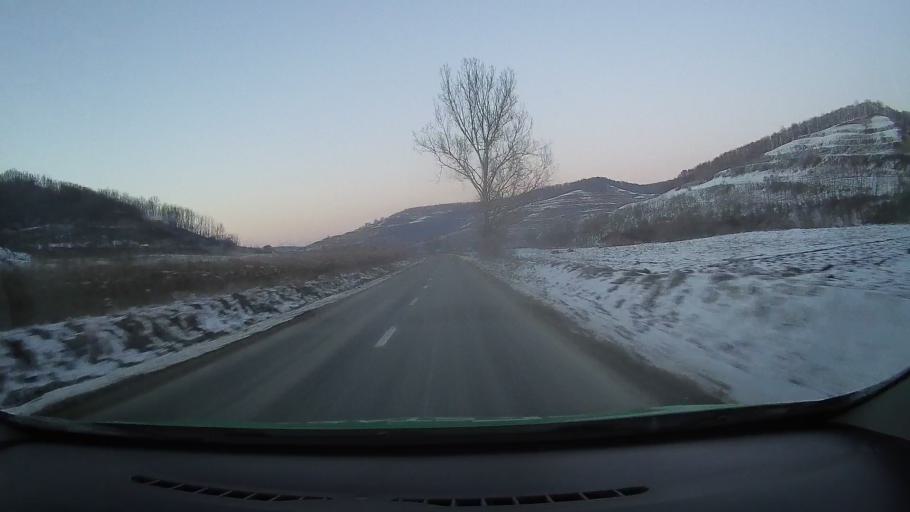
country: RO
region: Sibiu
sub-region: Comuna Atel
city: Atel
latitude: 46.1737
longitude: 24.4708
